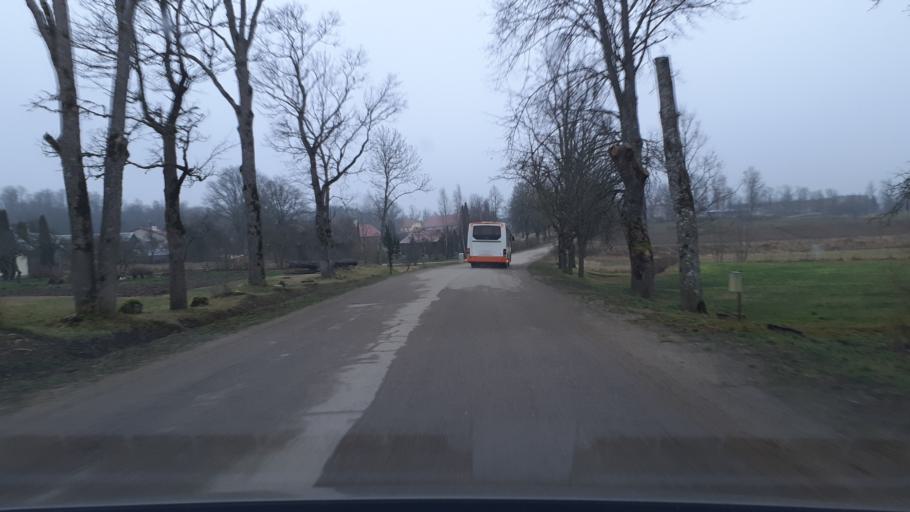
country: LV
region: Talsu Rajons
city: Sabile
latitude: 56.9545
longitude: 22.3944
